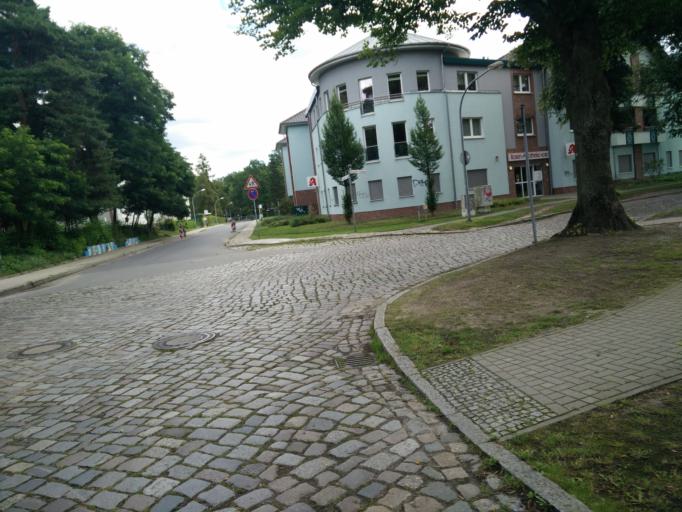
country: DE
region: Brandenburg
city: Falkensee
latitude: 52.5738
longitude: 13.0912
